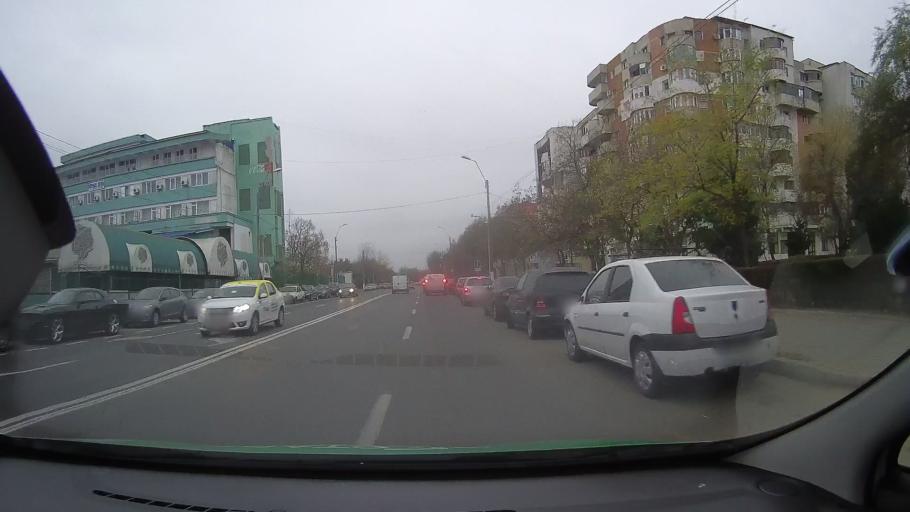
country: RO
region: Ialomita
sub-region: Comuna Slobozia
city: Slobozia
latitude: 44.5680
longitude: 27.3847
